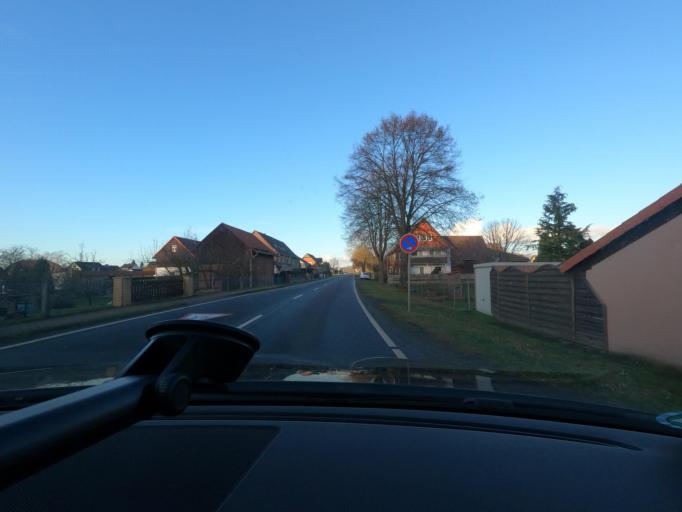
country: DE
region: Lower Saxony
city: Rhumspringe
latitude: 51.6106
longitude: 10.3225
